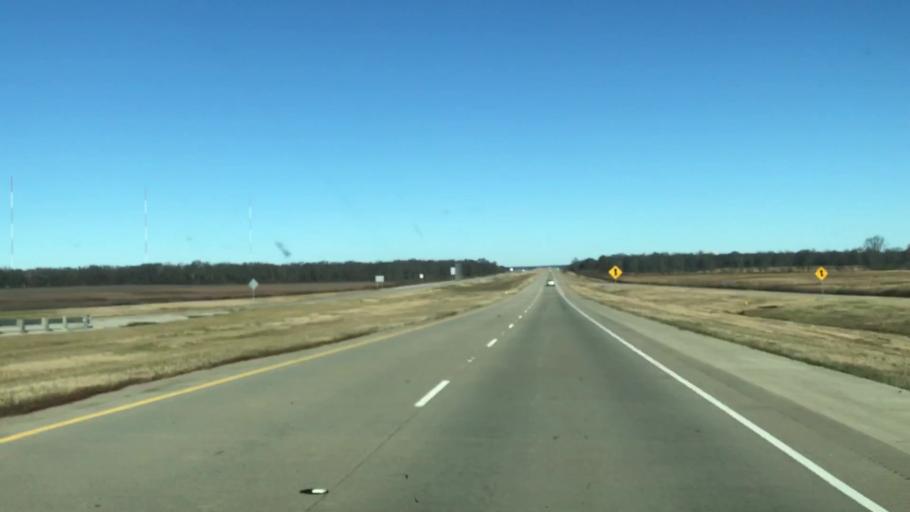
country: US
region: Louisiana
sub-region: Caddo Parish
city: Blanchard
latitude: 32.6770
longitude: -93.8509
